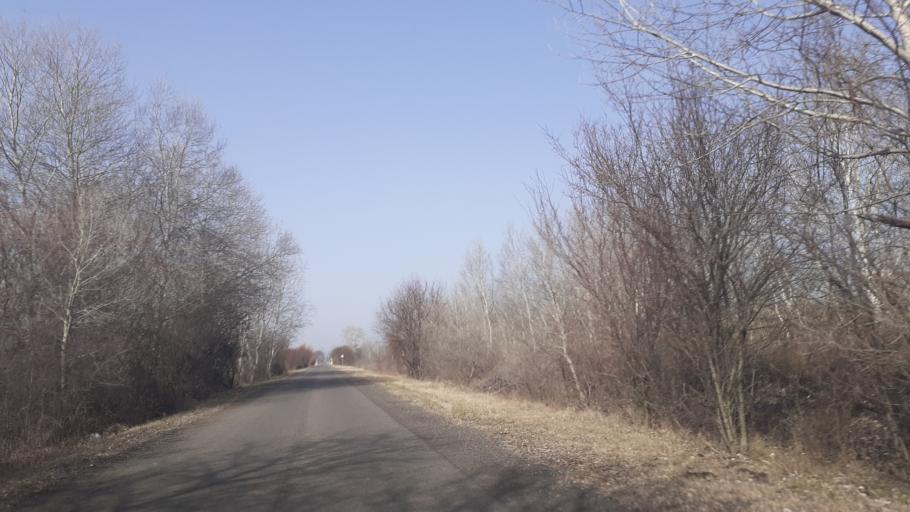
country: HU
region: Pest
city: Dabas
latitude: 47.1130
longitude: 19.2198
